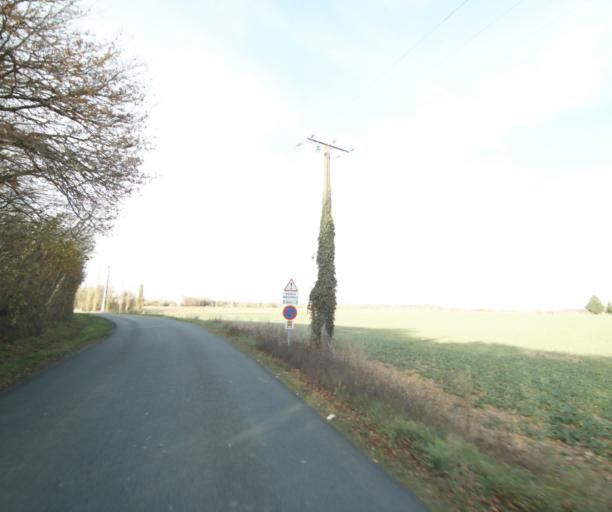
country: FR
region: Poitou-Charentes
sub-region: Departement de la Charente-Maritime
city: Saint-Hilaire-de-Villefranche
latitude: 45.8101
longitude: -0.5570
